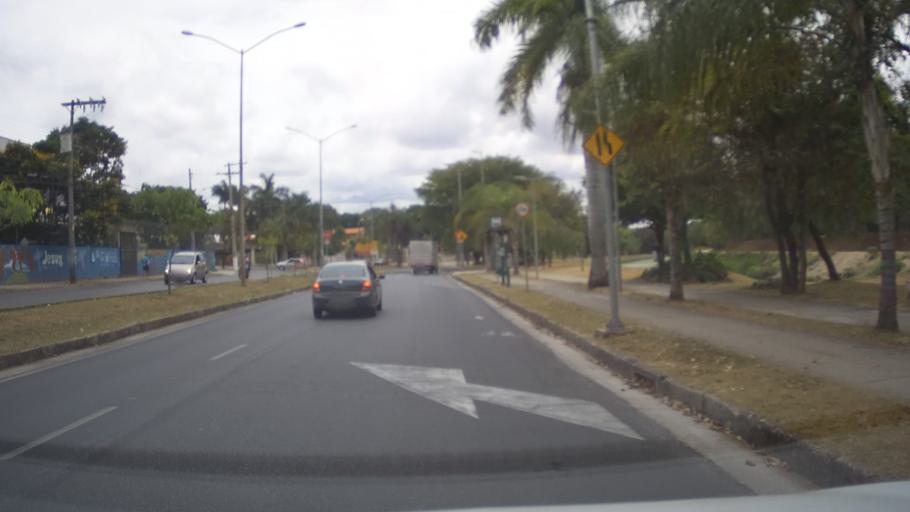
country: BR
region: Minas Gerais
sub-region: Belo Horizonte
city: Belo Horizonte
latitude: -19.8586
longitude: -43.9981
